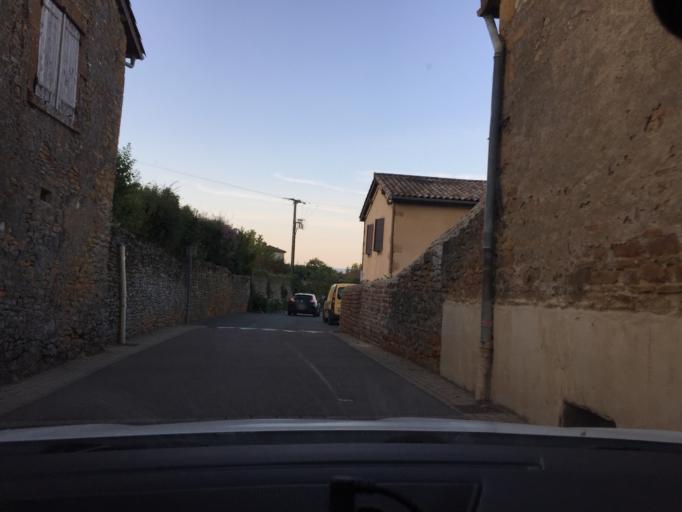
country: FR
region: Rhone-Alpes
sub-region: Departement du Rhone
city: Charnay
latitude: 45.8900
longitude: 4.6671
